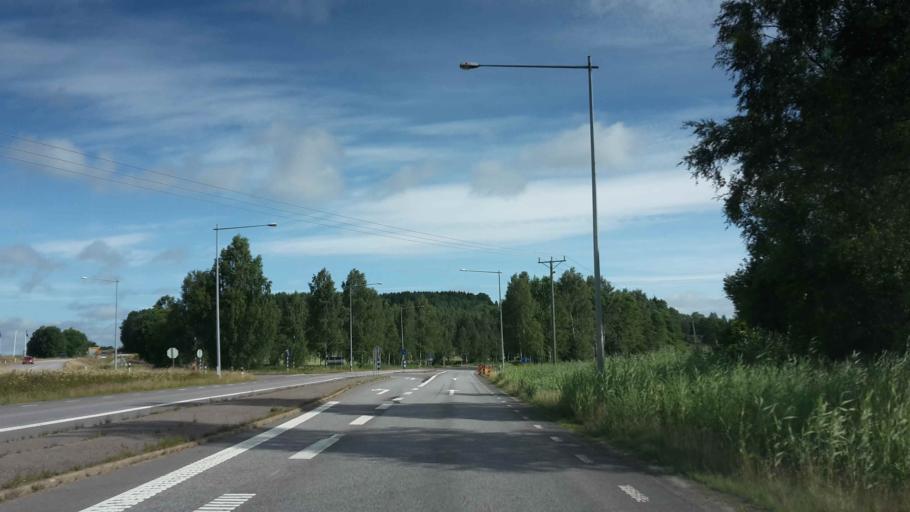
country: SE
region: OErebro
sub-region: Askersunds Kommun
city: Askersund
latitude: 58.8880
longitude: 14.8999
